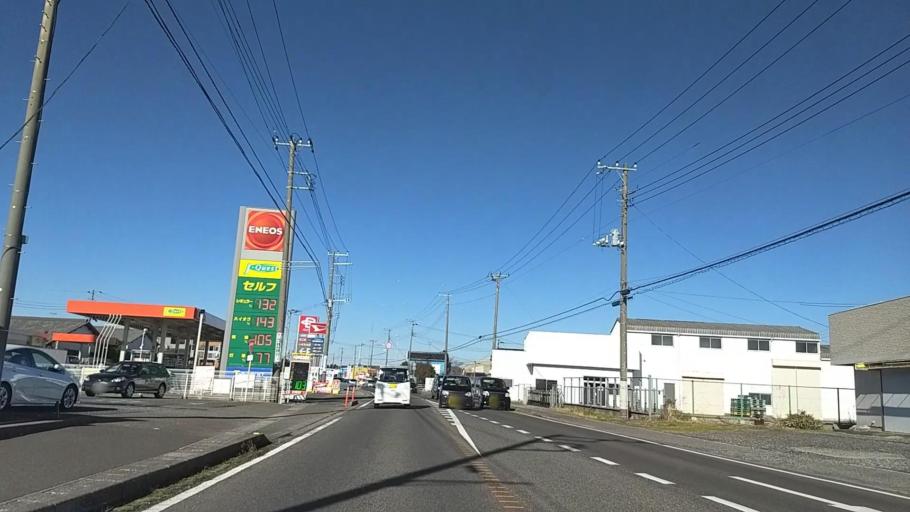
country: JP
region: Chiba
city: Ohara
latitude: 35.2754
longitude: 140.3941
